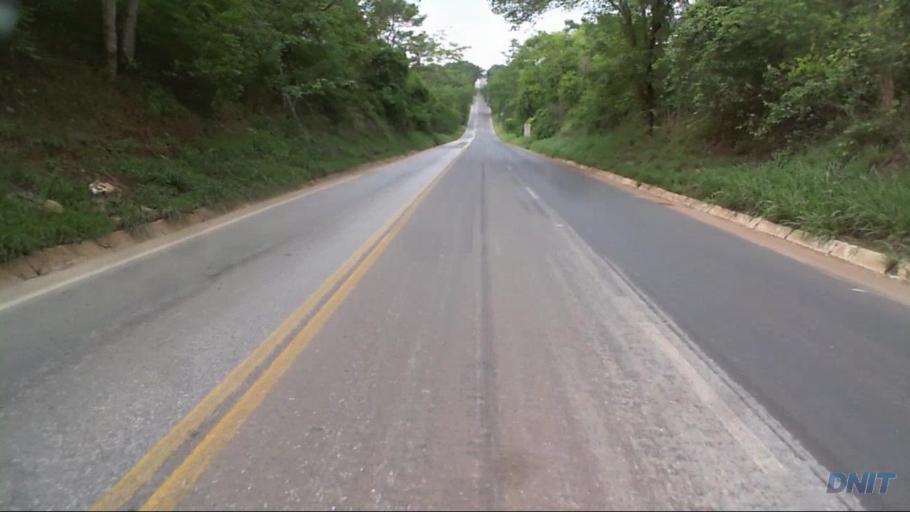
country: BR
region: Goias
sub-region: Uruacu
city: Uruacu
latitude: -14.5999
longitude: -49.1650
